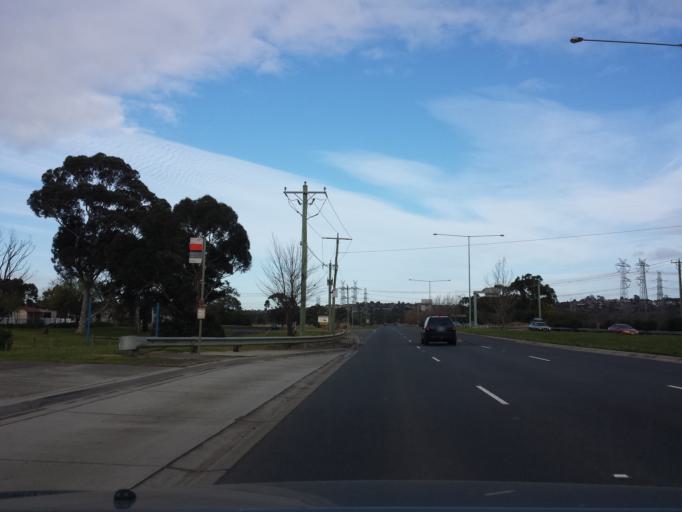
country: AU
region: Victoria
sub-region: Monash
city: Mulgrave
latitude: -37.9038
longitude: 145.2141
